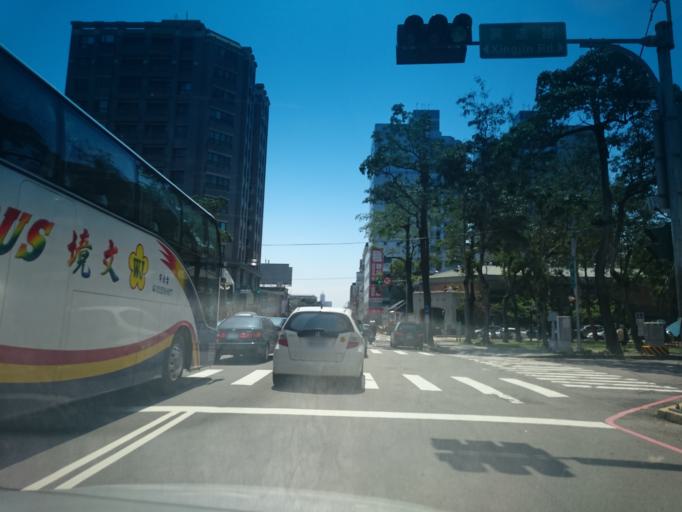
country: TW
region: Taiwan
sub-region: Taichung City
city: Taichung
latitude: 24.1568
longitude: 120.6903
